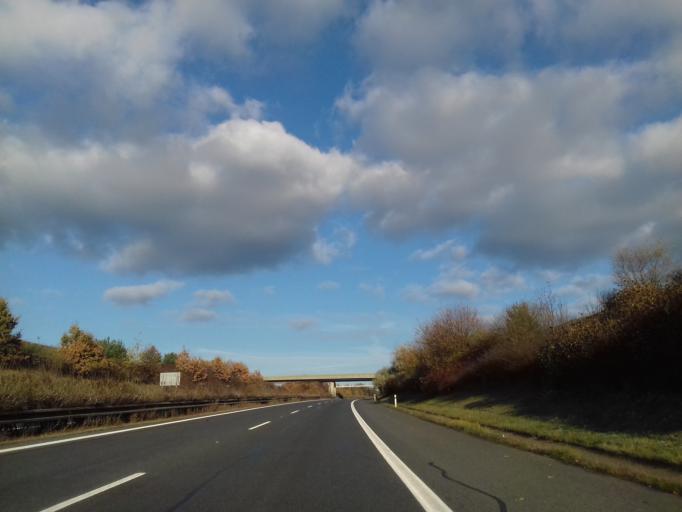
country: CZ
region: Plzensky
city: Stary Plzenec
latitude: 49.7206
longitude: 13.4603
